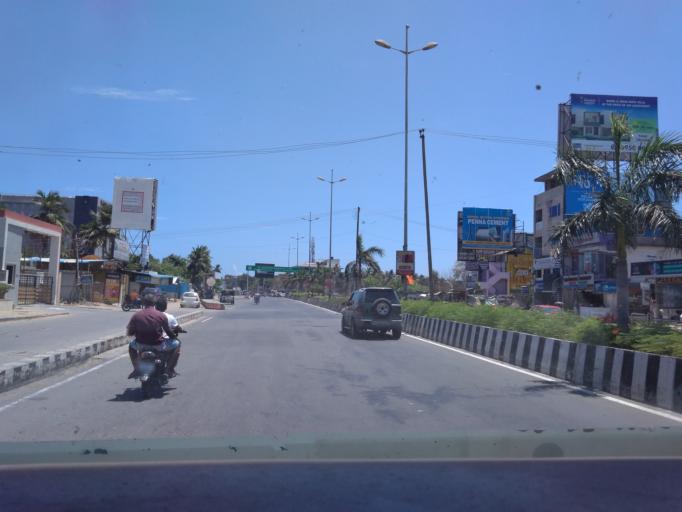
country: IN
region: Tamil Nadu
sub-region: Kancheepuram
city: Injambakkam
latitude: 12.8335
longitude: 80.2289
